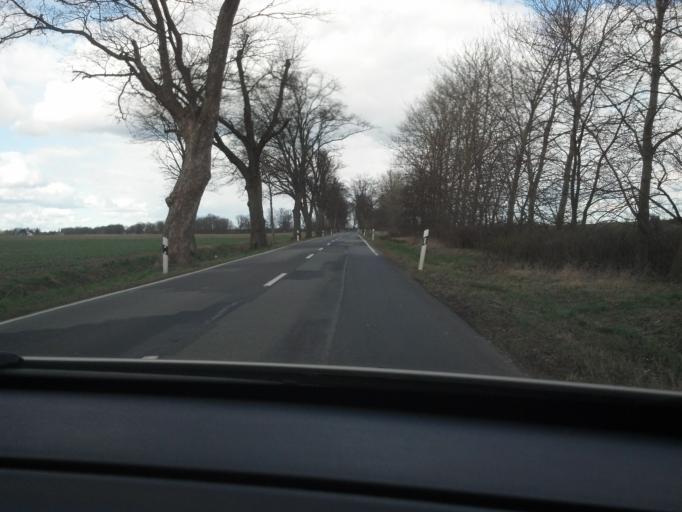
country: DE
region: Mecklenburg-Vorpommern
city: Loitz
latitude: 53.4248
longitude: 13.3541
